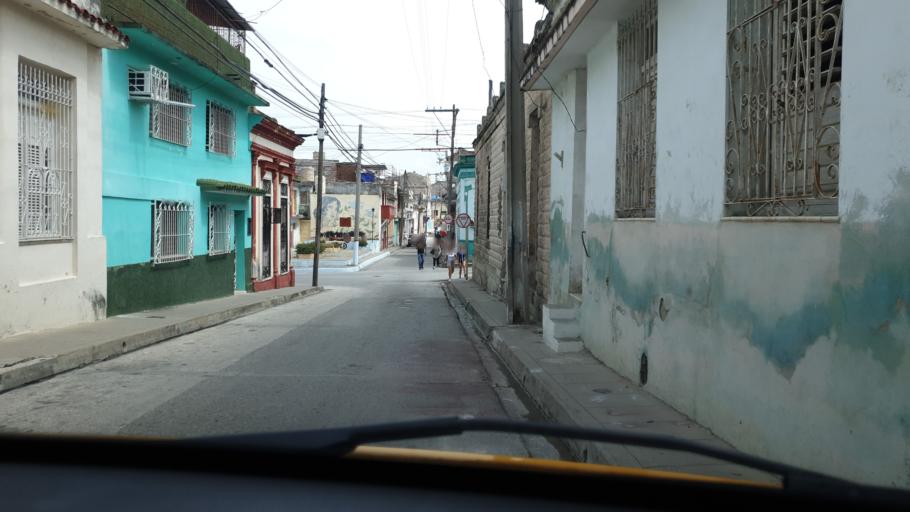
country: CU
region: Villa Clara
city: Santa Clara
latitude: 22.4033
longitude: -79.9652
